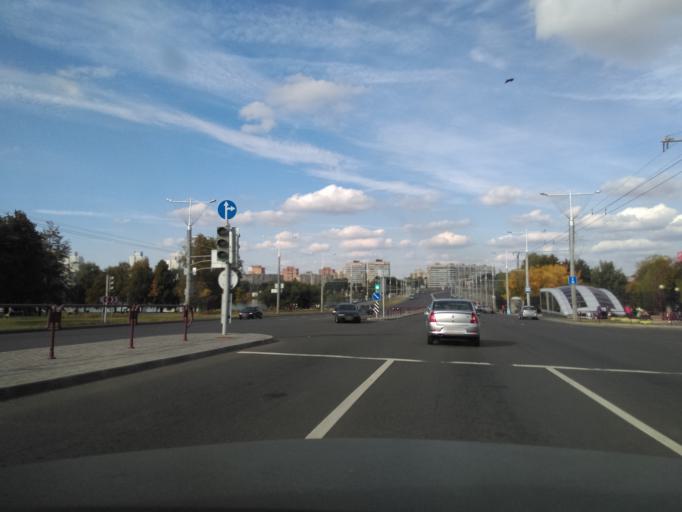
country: BY
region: Minsk
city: Hatava
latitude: 53.8491
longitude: 27.6330
